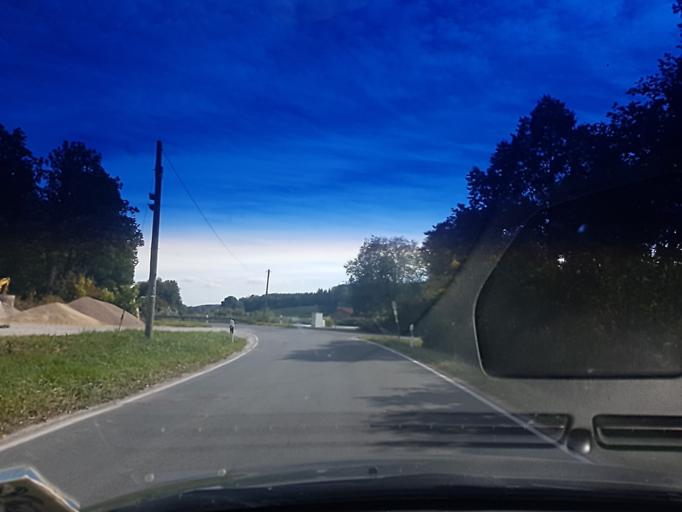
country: DE
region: Bavaria
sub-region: Regierungsbezirk Mittelfranken
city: Wachenroth
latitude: 49.7826
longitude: 10.7015
